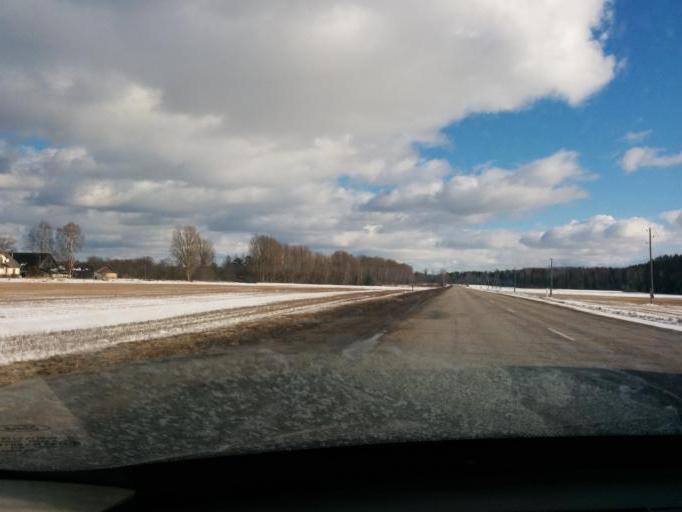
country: LV
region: Cesvaine
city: Cesvaine
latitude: 57.2384
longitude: 26.4080
